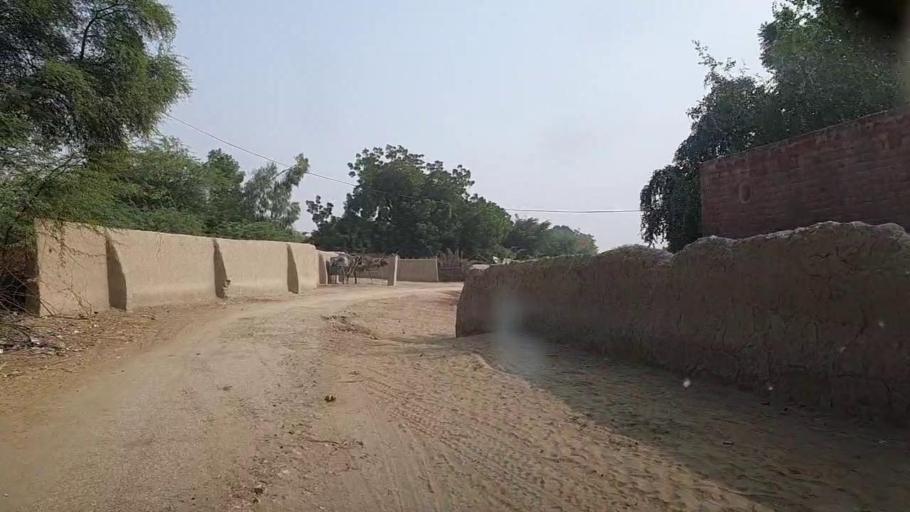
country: PK
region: Sindh
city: Bozdar
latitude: 27.0594
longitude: 68.6527
